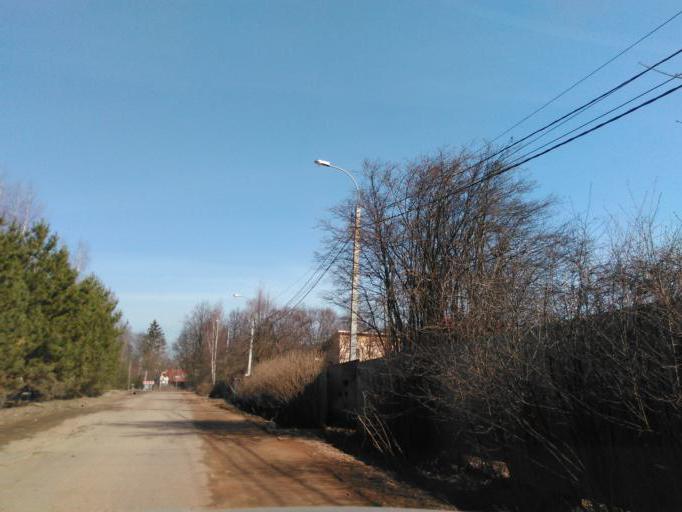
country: RU
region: Moskovskaya
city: Opalikha
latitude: 55.8854
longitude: 37.2638
